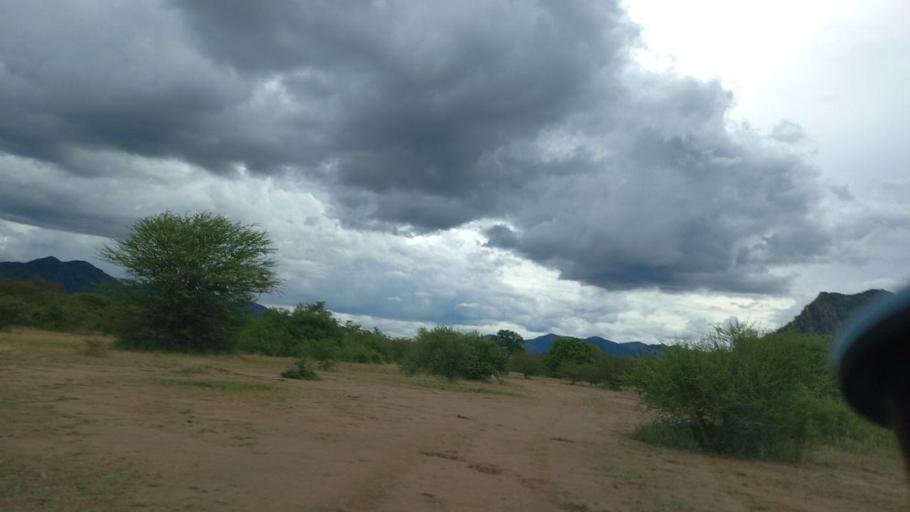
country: ZM
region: Lusaka
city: Luangwa
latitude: -15.6170
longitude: 30.2713
